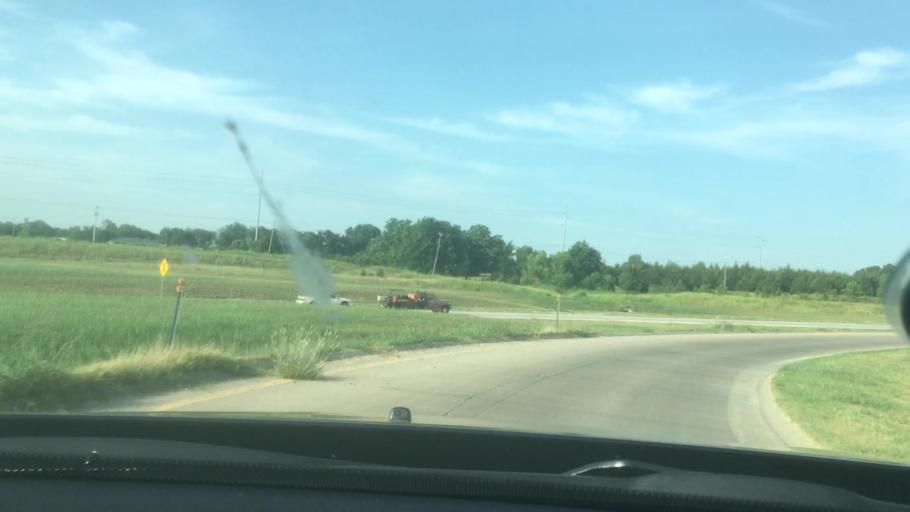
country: US
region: Oklahoma
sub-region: Pontotoc County
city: Ada
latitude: 34.7531
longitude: -96.6711
